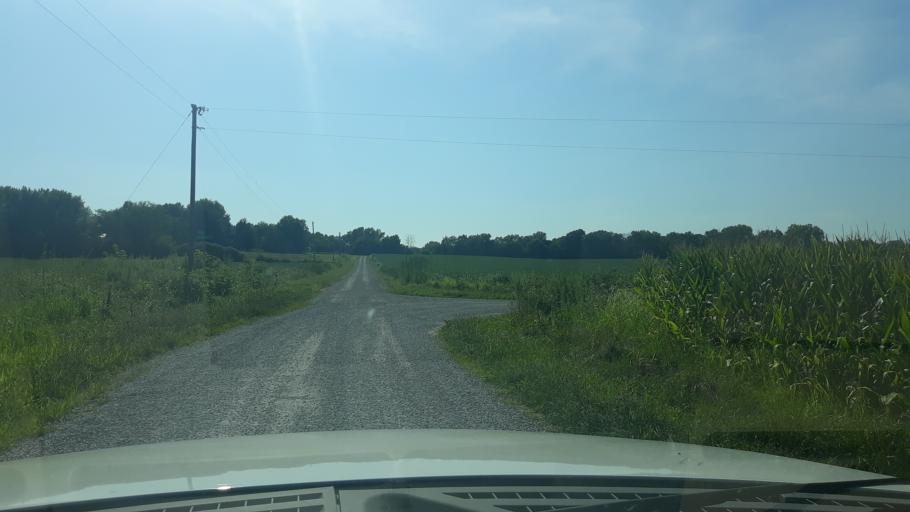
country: US
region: Illinois
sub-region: Saline County
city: Eldorado
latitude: 37.8468
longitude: -88.4845
